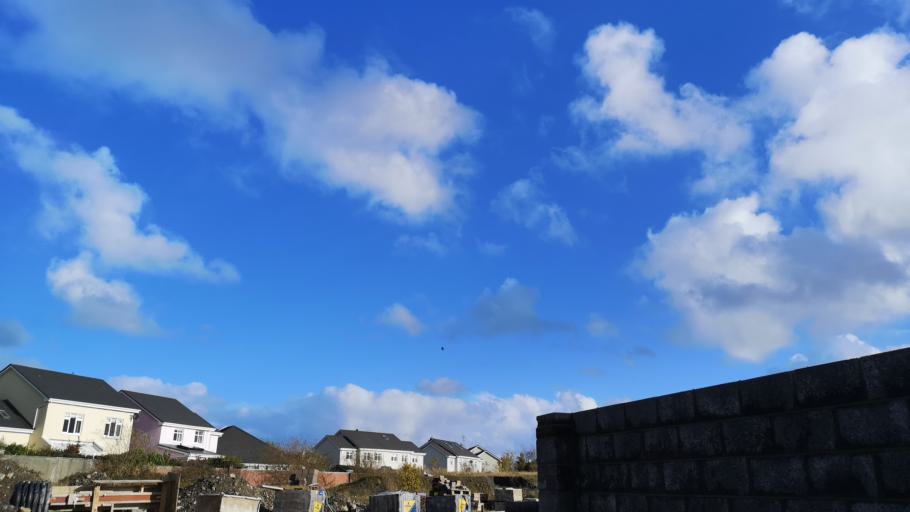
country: IE
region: Connaught
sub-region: County Galway
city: Athenry
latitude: 53.3016
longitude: -8.7597
